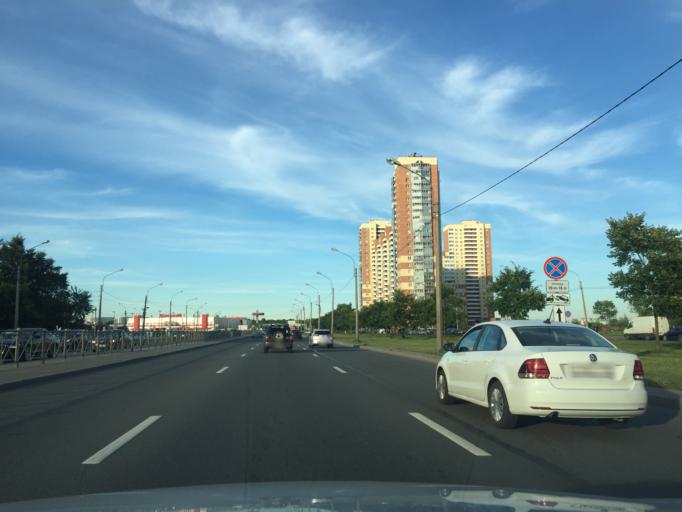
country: RU
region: St.-Petersburg
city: Obukhovo
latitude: 59.8431
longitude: 30.4133
